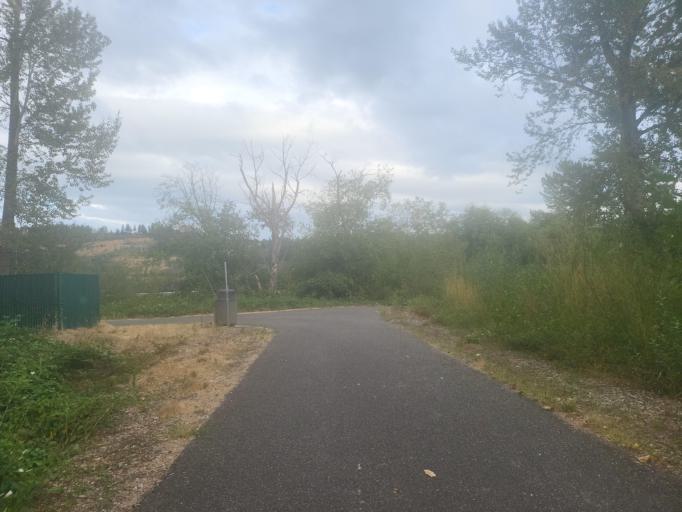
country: US
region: Washington
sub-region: King County
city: Pacific
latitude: 47.2428
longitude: -122.2359
